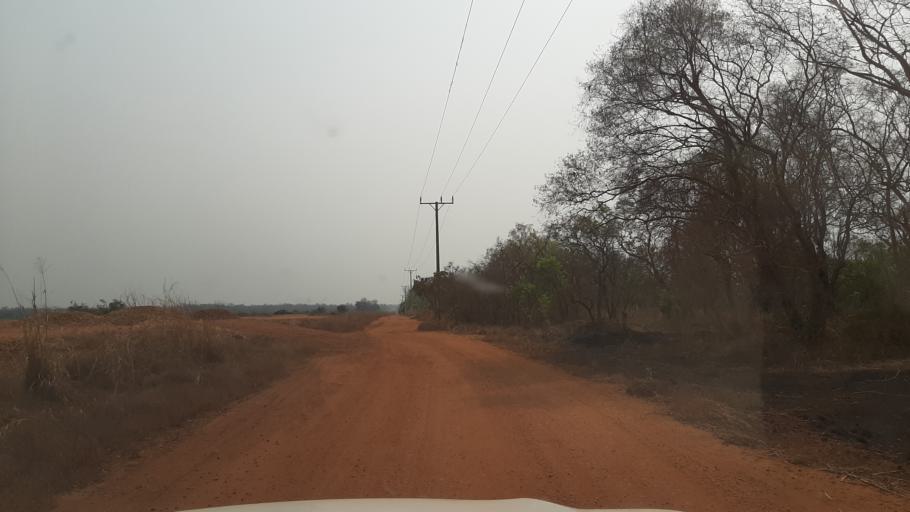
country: ET
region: Gambela
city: Gambela
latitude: 8.1551
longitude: 34.3062
